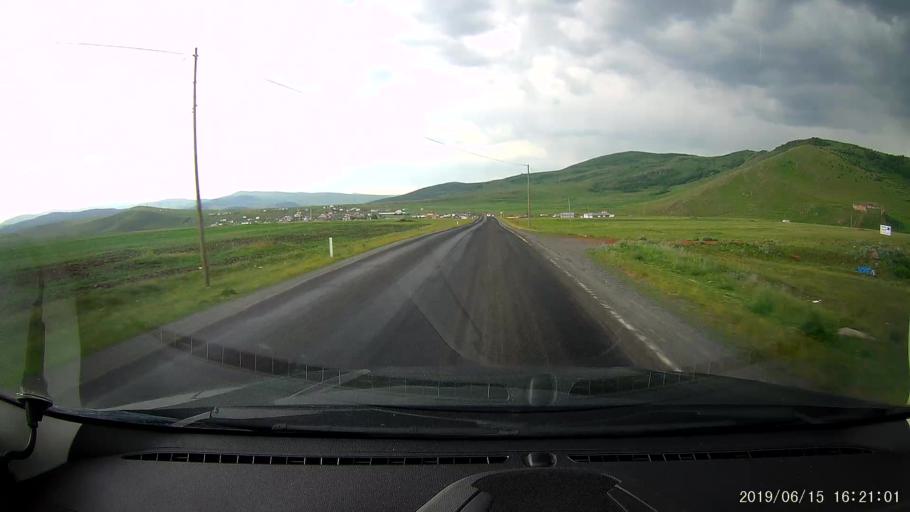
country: TR
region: Ardahan
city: Hanak
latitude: 41.2042
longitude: 42.8464
